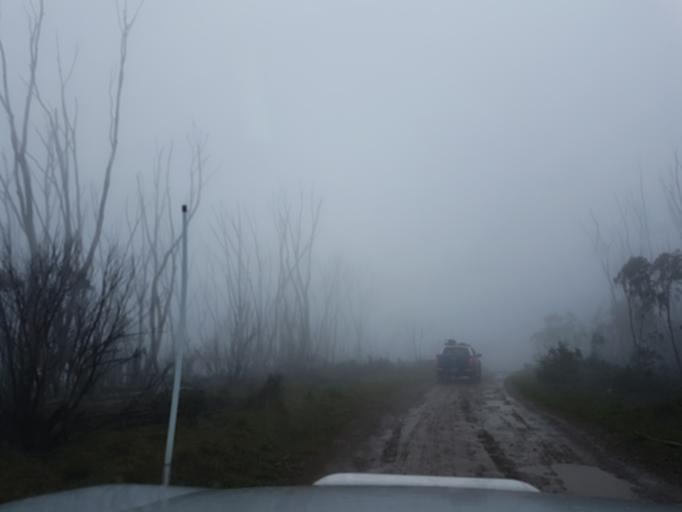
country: AU
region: Victoria
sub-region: Alpine
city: Mount Beauty
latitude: -37.0891
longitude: 147.0854
